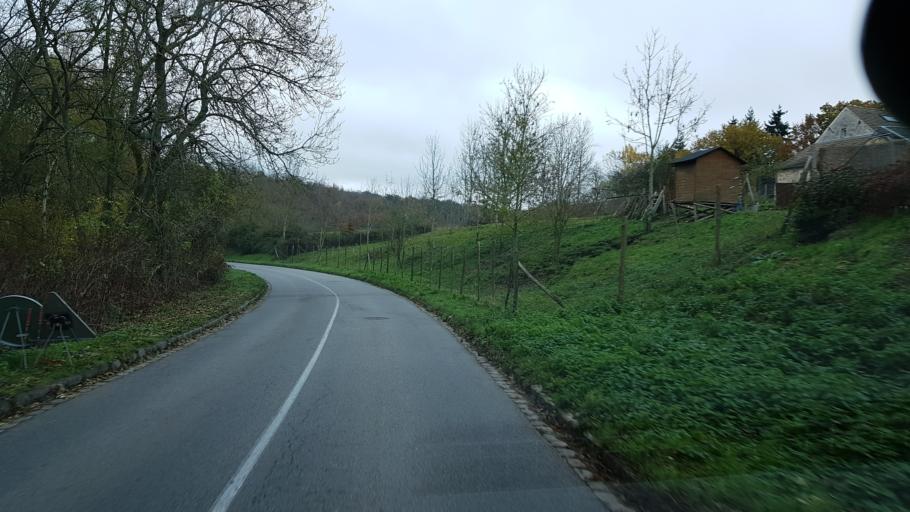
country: FR
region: Ile-de-France
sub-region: Departement des Yvelines
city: Chevreuse
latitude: 48.7174
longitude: 2.0159
